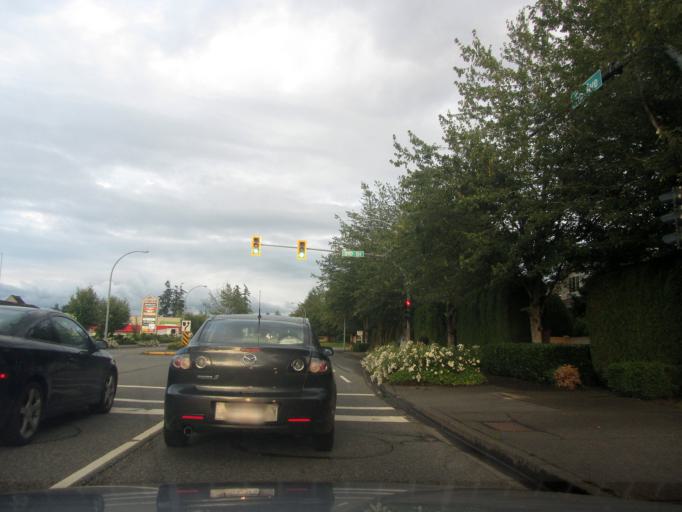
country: CA
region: British Columbia
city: Walnut Grove
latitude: 49.1623
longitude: -122.6379
